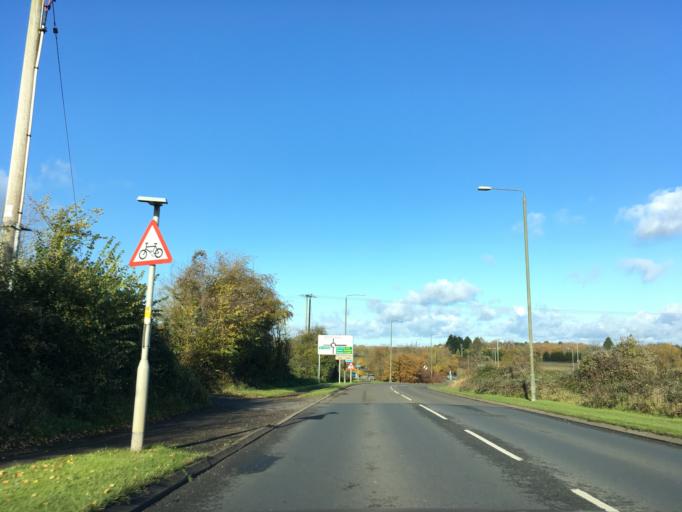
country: GB
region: England
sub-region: Worcestershire
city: Evesham
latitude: 52.1120
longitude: -1.9445
